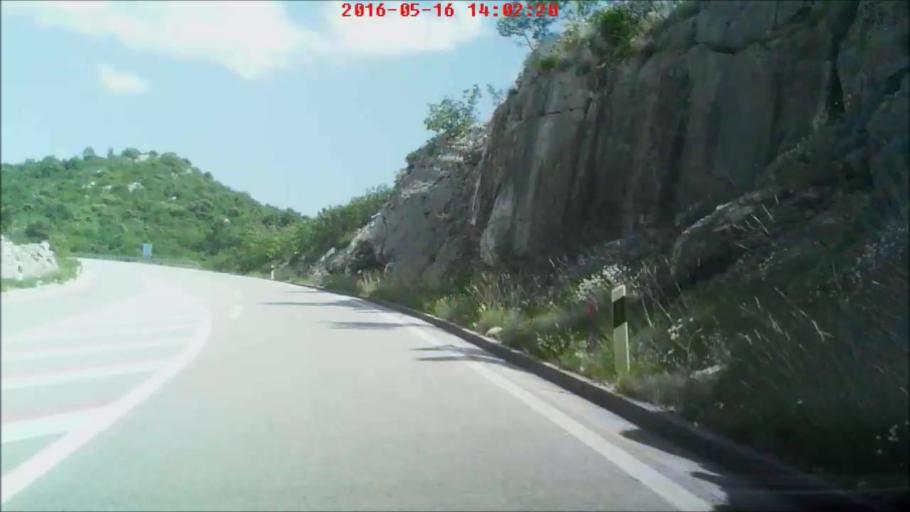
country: HR
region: Dubrovacko-Neretvanska
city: Ston
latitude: 42.8256
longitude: 17.7571
